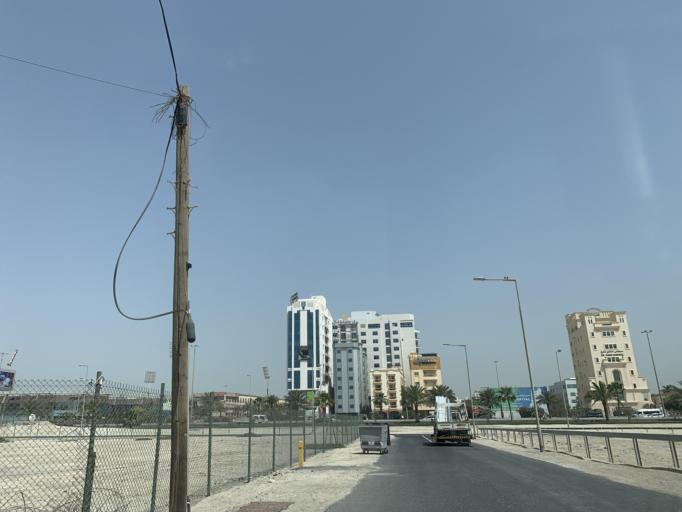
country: BH
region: Manama
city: Manama
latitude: 26.2029
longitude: 50.5764
